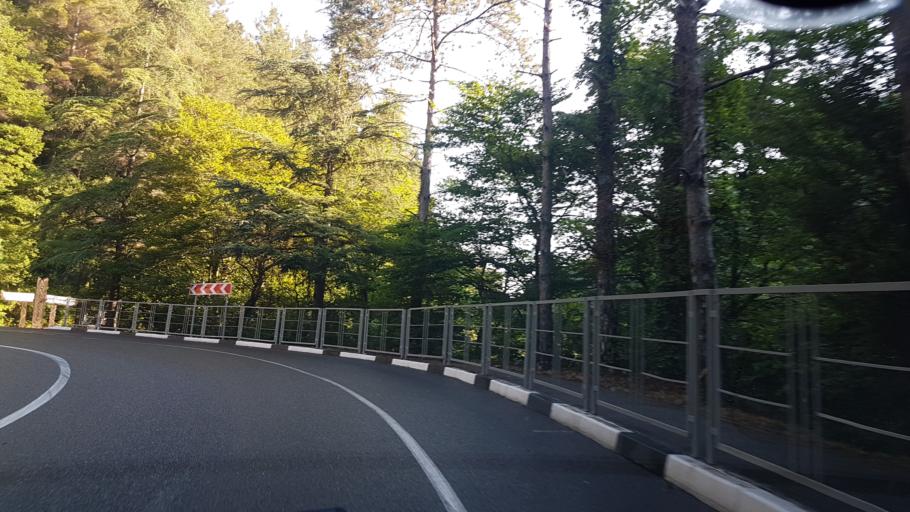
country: RU
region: Krasnodarskiy
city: Vardane
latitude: 43.8035
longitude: 39.4554
